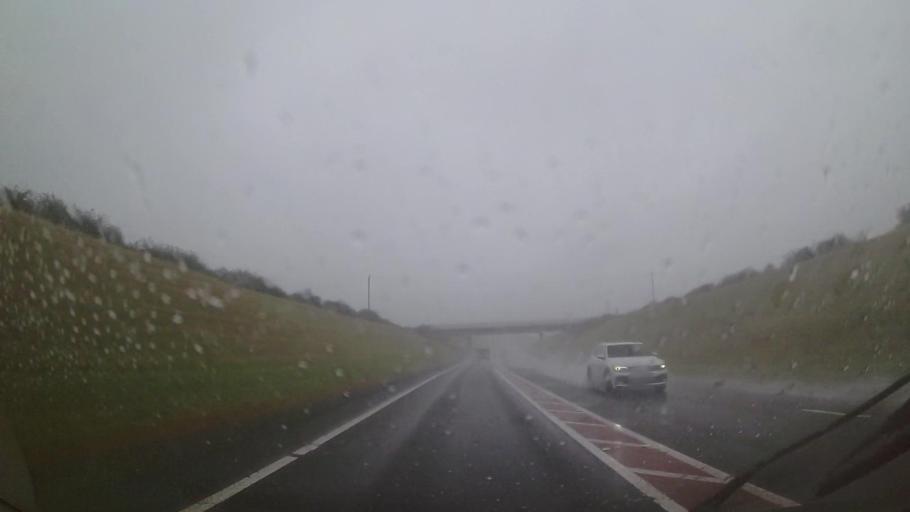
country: GB
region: Wales
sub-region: Carmarthenshire
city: Whitland
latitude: 51.7785
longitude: -4.6071
